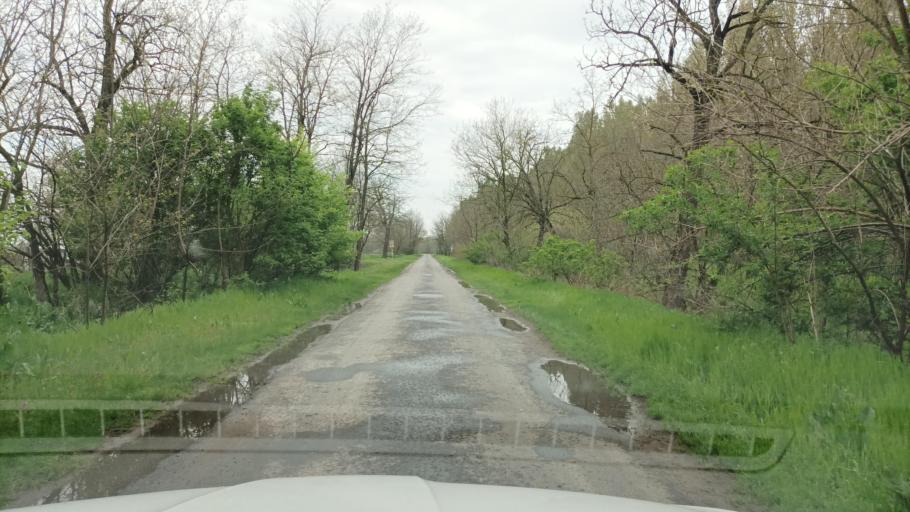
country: HU
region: Pest
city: Nagykoros
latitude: 46.9731
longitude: 19.8161
